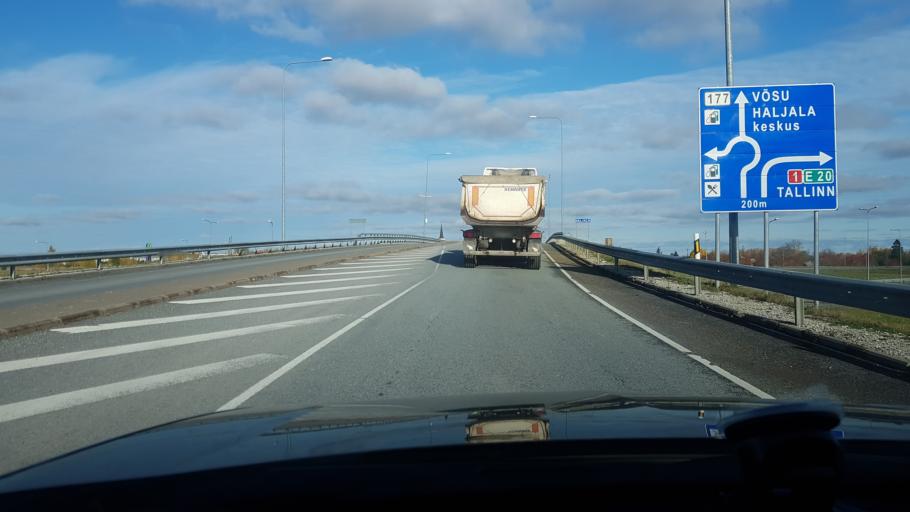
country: EE
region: Laeaene-Virumaa
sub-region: Haljala vald
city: Haljala
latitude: 59.4230
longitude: 26.2697
